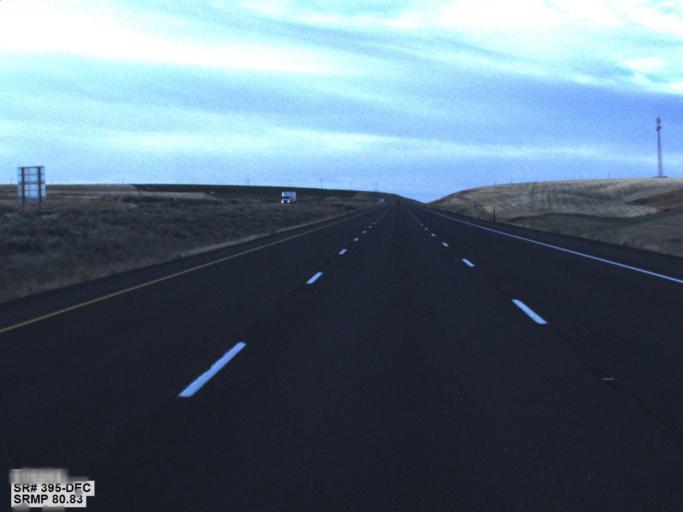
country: US
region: Washington
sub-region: Adams County
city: Ritzville
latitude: 46.9518
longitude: -118.5770
